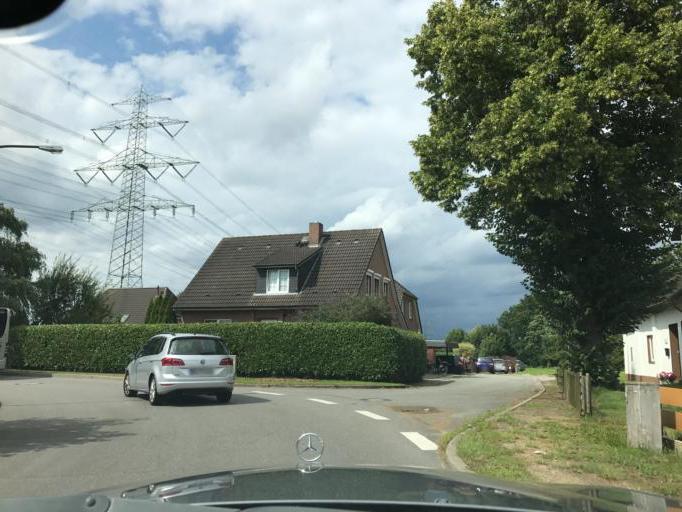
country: DE
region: Schleswig-Holstein
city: Oststeinbek
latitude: 53.5230
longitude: 10.1636
